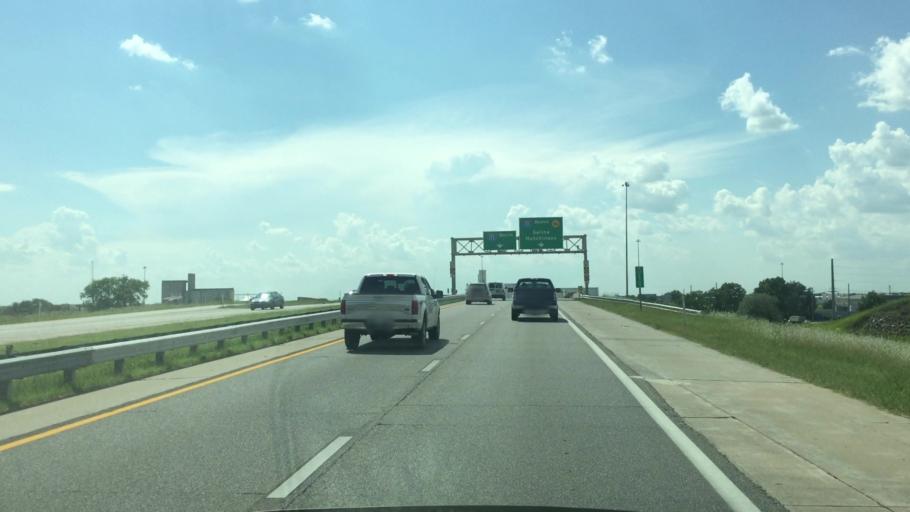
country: US
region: Kansas
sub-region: Sedgwick County
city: Bellaire
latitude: 37.7430
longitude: -97.3136
